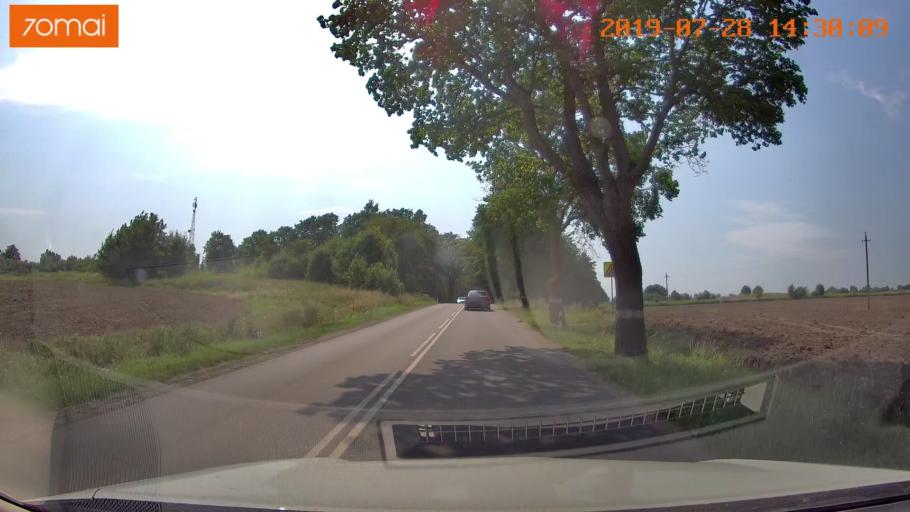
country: RU
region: Kaliningrad
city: Primorsk
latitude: 54.8051
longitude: 20.0608
